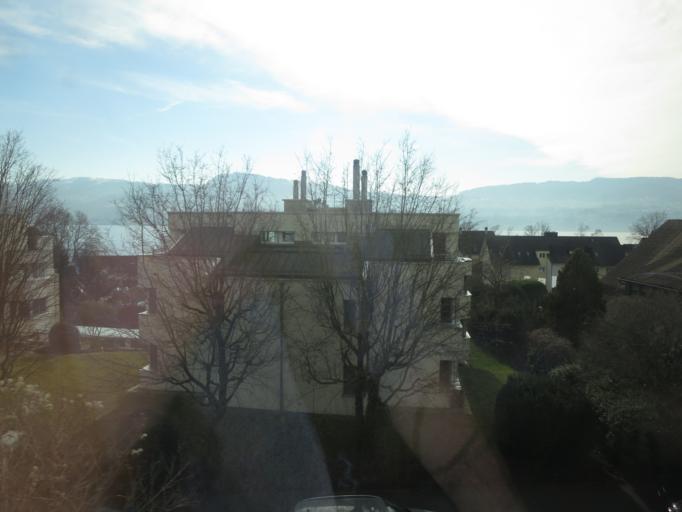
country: CH
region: Zurich
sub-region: Bezirk Meilen
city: Dorf
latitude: 47.2356
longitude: 8.7389
